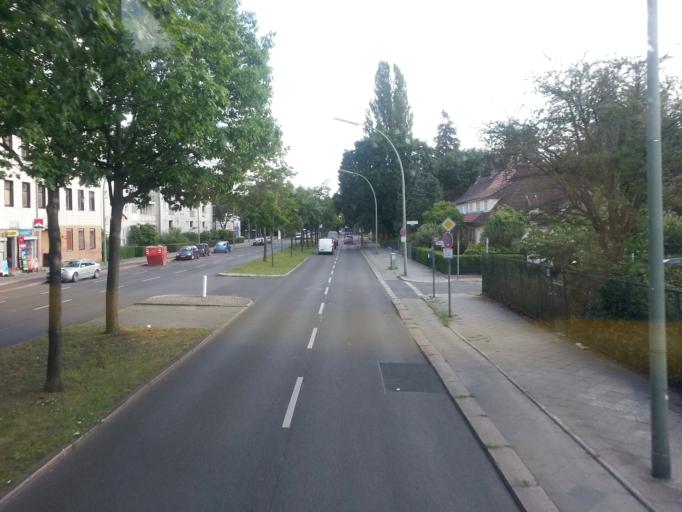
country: DE
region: Berlin
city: Reinickendorf
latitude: 52.5828
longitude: 13.3342
